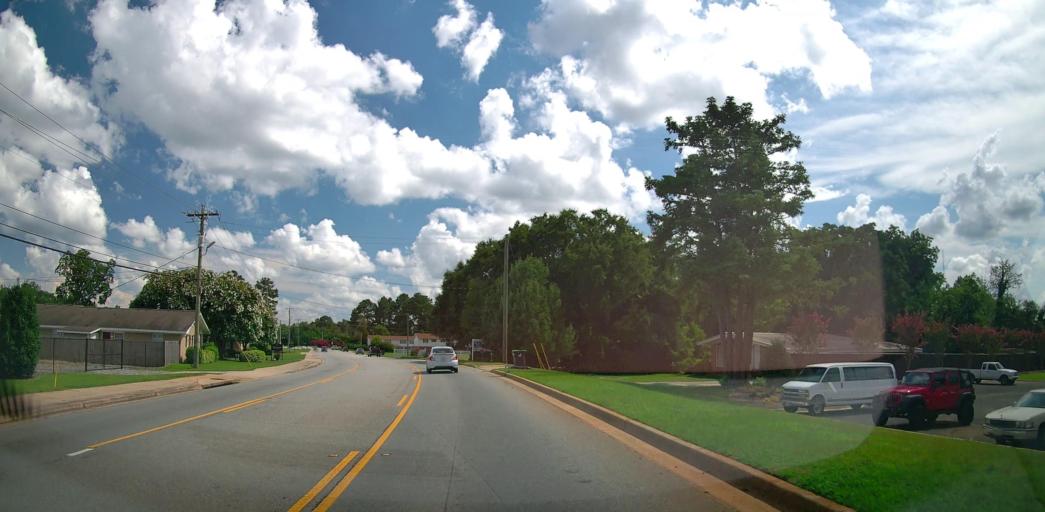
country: US
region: Georgia
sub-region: Houston County
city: Centerville
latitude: 32.6048
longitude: -83.6609
